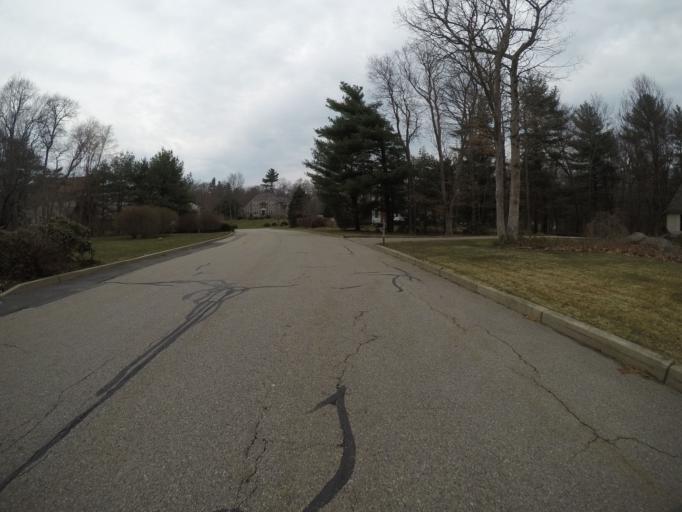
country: US
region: Massachusetts
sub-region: Norfolk County
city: Stoughton
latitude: 42.0851
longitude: -71.1026
